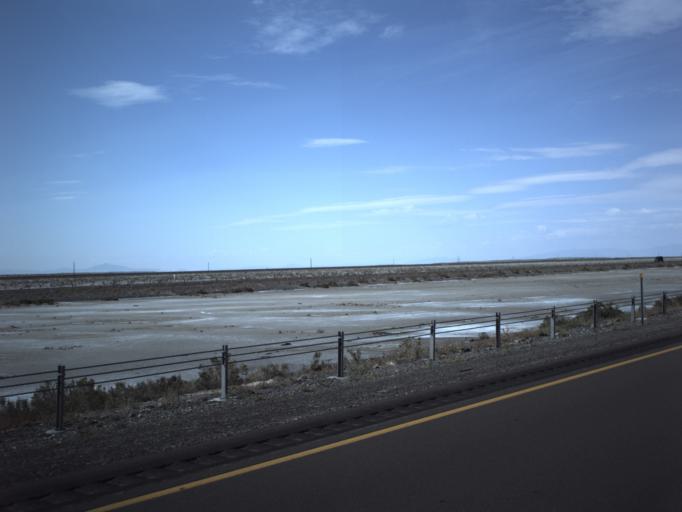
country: US
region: Utah
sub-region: Tooele County
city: Wendover
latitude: 40.7283
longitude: -113.3148
